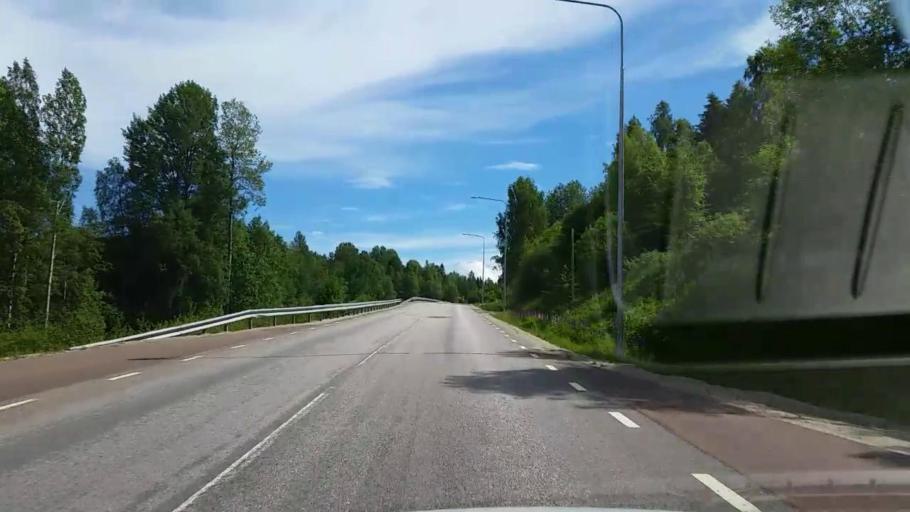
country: SE
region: Gaevleborg
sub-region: Bollnas Kommun
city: Vittsjo
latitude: 61.1559
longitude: 15.8840
